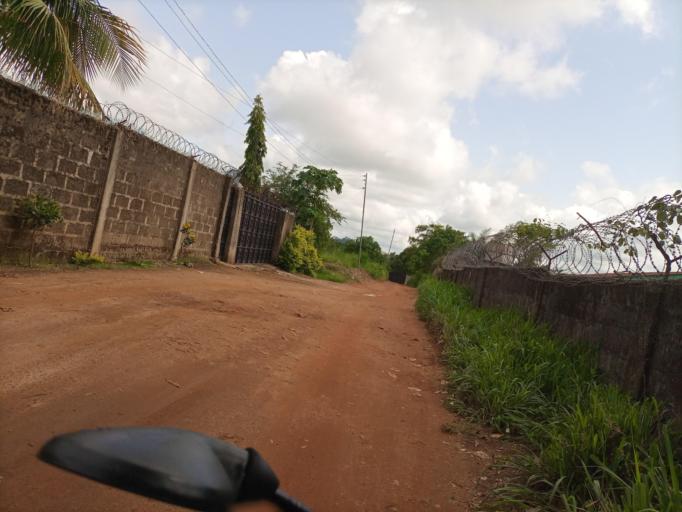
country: SL
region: Southern Province
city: Bo
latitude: 7.9690
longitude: -11.7631
